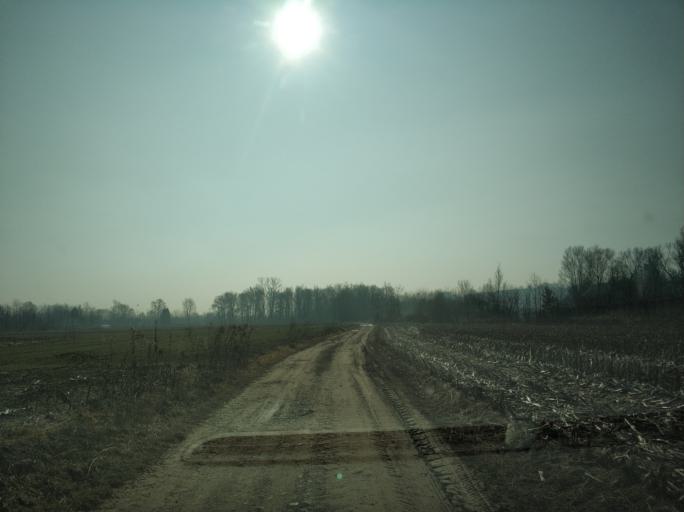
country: IT
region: Piedmont
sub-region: Provincia di Torino
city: Lombardore
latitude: 45.2474
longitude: 7.7363
